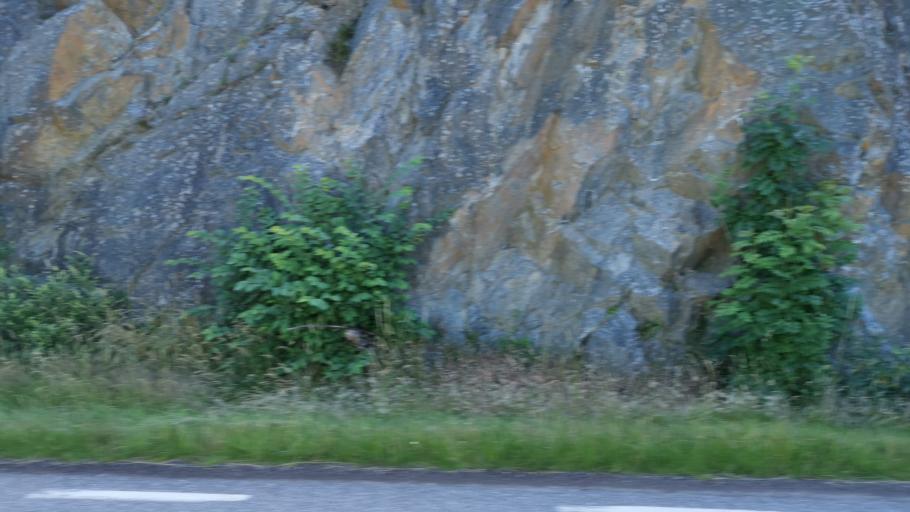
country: SE
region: Vaestra Goetaland
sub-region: Lysekils Kommun
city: Lysekil
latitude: 58.2327
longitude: 11.4548
